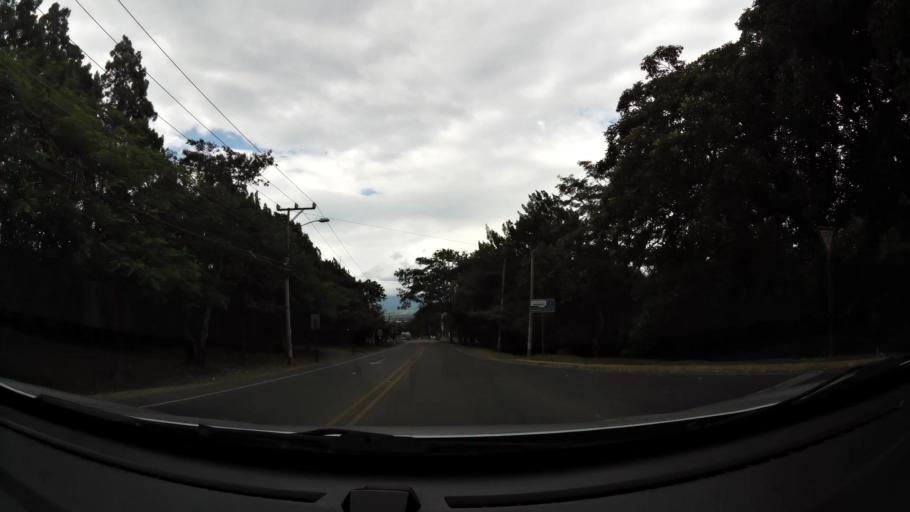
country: CR
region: San Jose
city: Santa Ana
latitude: 9.9380
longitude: -84.1888
